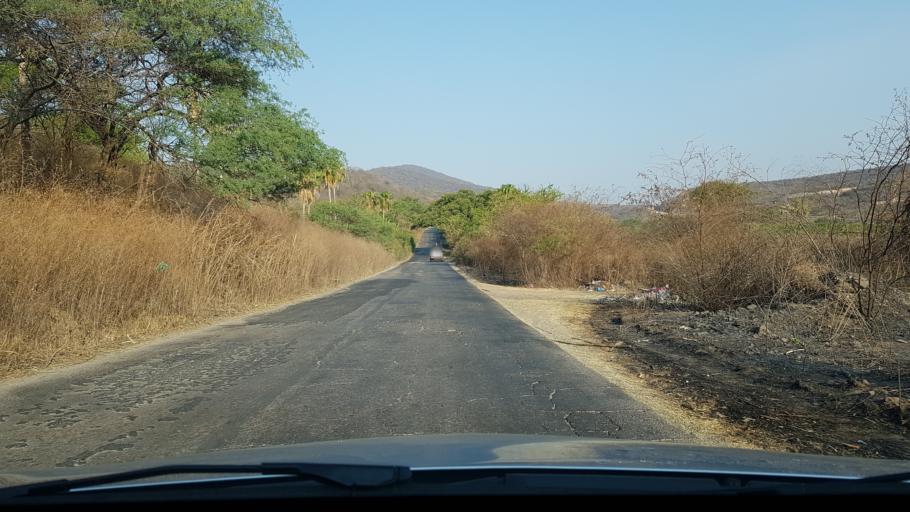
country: MX
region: Morelos
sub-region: Tepalcingo
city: Zacapalco
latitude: 18.6531
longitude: -99.0336
